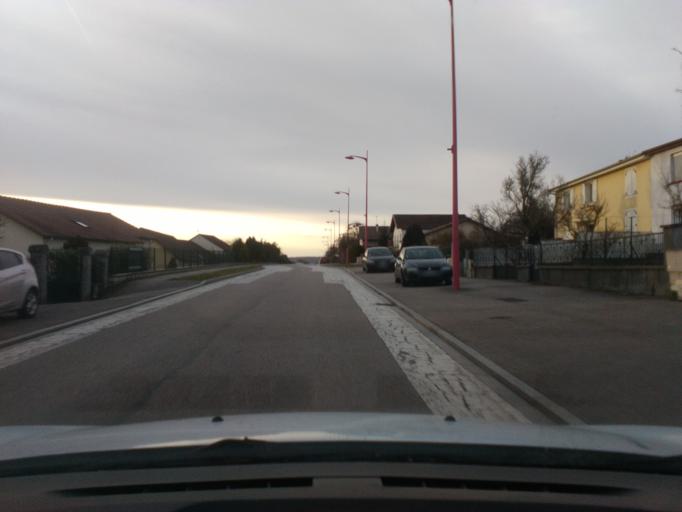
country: FR
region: Lorraine
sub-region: Departement des Vosges
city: Charmes
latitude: 48.3708
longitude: 6.3139
